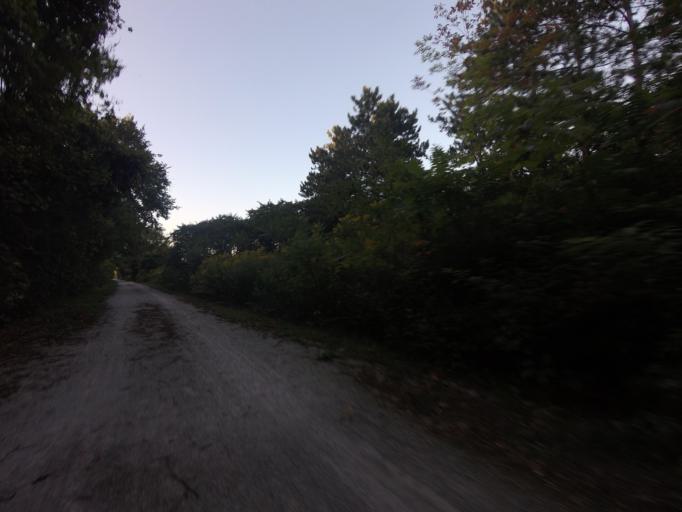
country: CA
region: Ontario
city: Brampton
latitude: 43.8931
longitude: -79.8376
